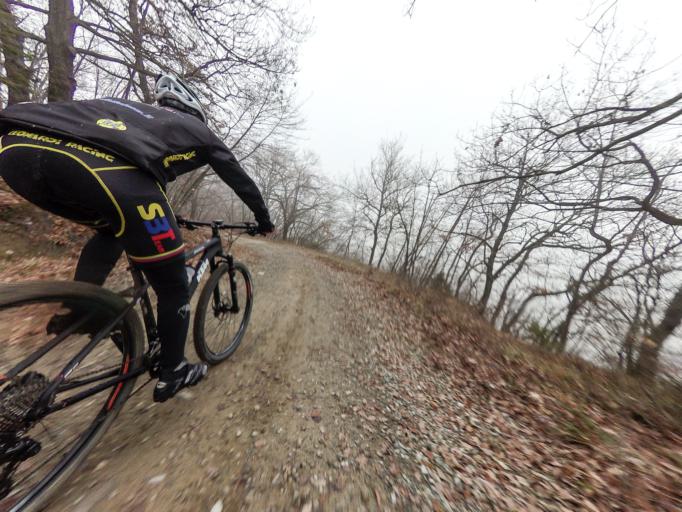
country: IT
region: Emilia-Romagna
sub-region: Provincia di Bologna
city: Pianoro
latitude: 44.3341
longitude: 11.3255
